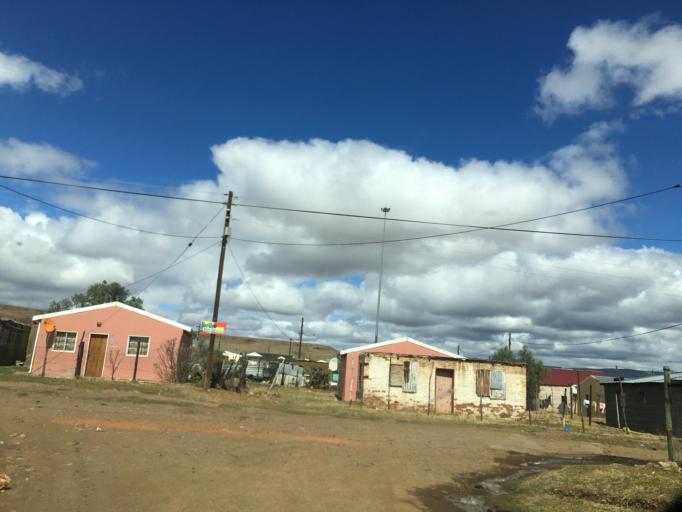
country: ZA
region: Eastern Cape
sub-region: Chris Hani District Municipality
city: Cala
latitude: -31.5348
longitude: 27.7021
